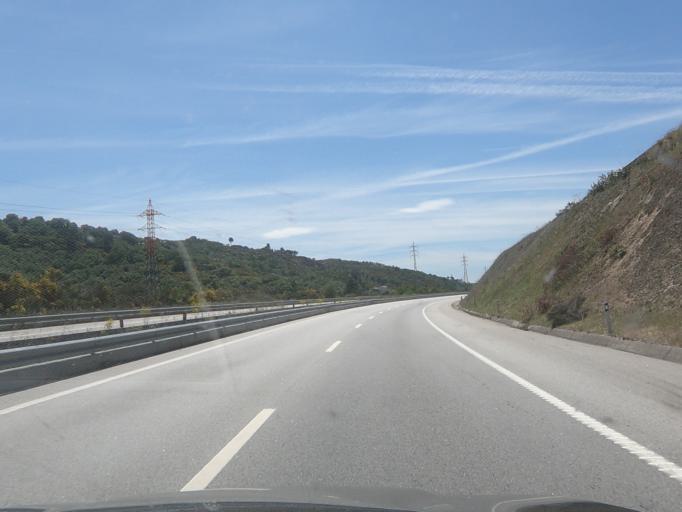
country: PT
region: Guarda
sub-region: Guarda
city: Sequeira
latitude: 40.5867
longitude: -7.2553
